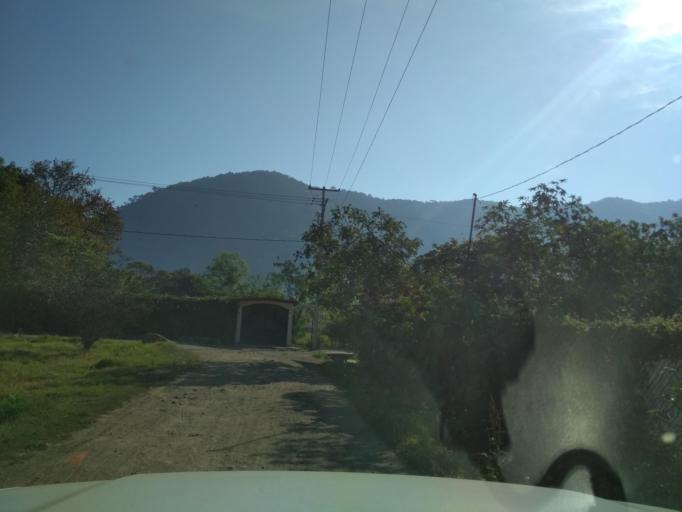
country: MX
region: Veracruz
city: Jalapilla
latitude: 18.8261
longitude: -97.0763
